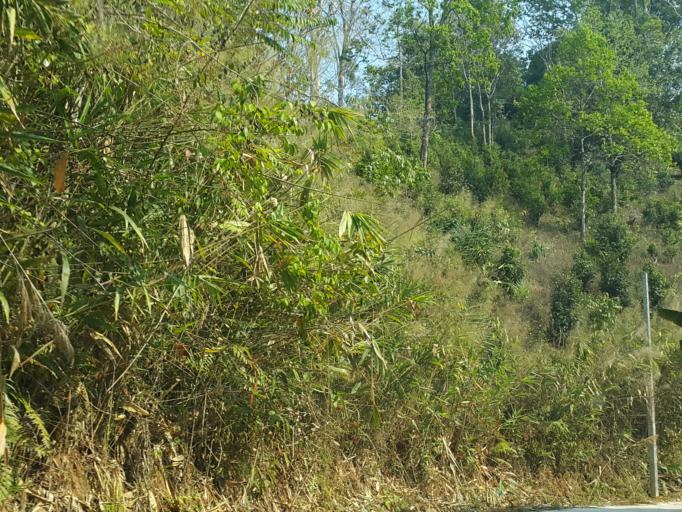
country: TH
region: Chiang Mai
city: Samoeng
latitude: 19.0157
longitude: 98.7597
